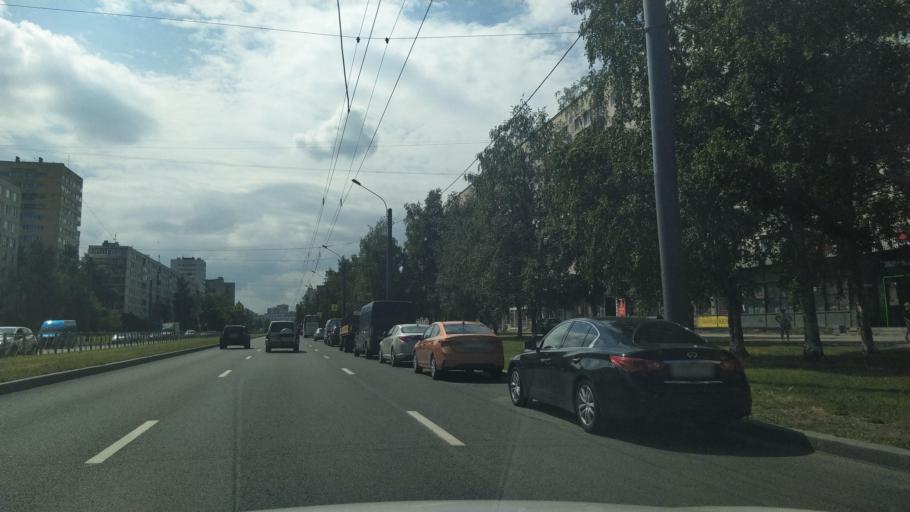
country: RU
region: Leningrad
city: Parnas
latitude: 60.0469
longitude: 30.3524
